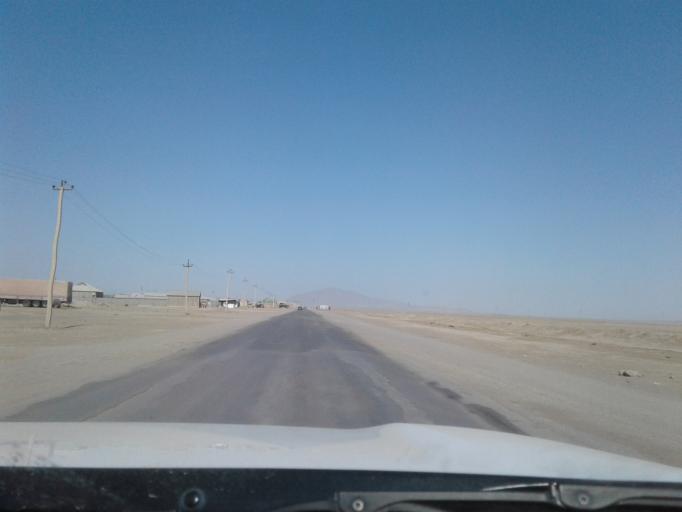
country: TM
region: Balkan
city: Gumdag
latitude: 39.1957
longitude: 54.5956
